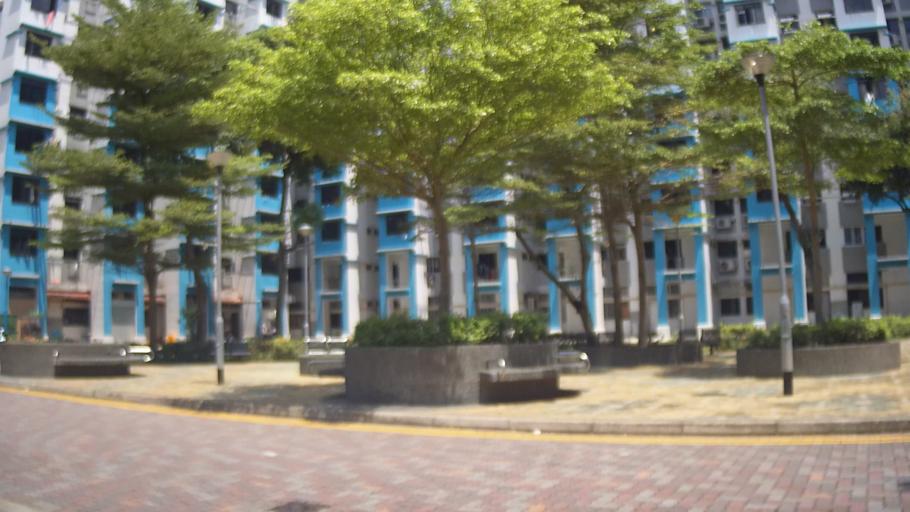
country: SG
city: Singapore
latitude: 1.3216
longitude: 103.8680
